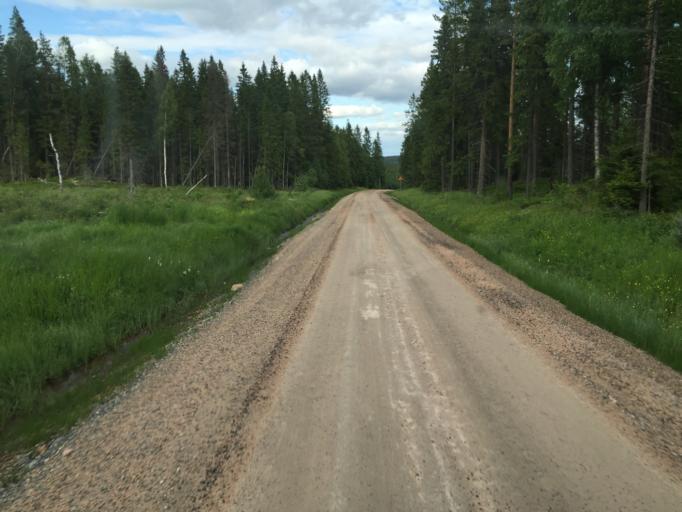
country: SE
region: Dalarna
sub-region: Malung-Saelens kommun
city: Malung
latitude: 60.8984
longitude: 13.7187
